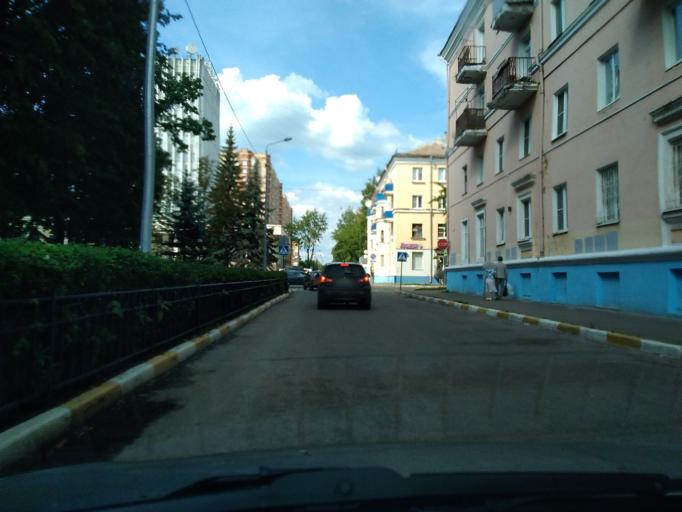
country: RU
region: Moskovskaya
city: Voskresensk
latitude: 55.3229
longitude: 38.6739
